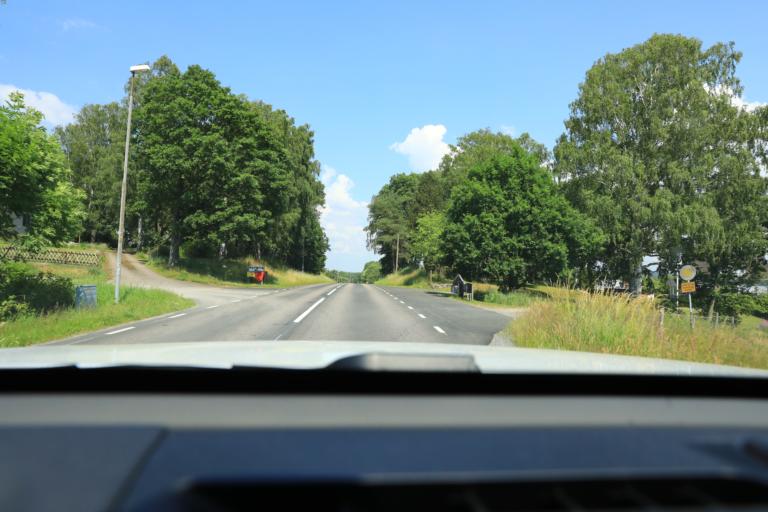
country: SE
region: Halland
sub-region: Varbergs Kommun
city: Veddige
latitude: 57.1945
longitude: 12.2880
